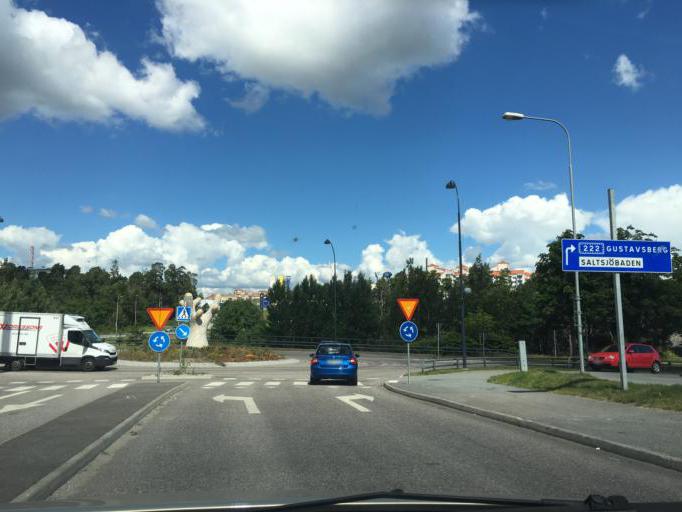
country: SE
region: Stockholm
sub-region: Nacka Kommun
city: Nacka
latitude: 59.3111
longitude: 18.1677
